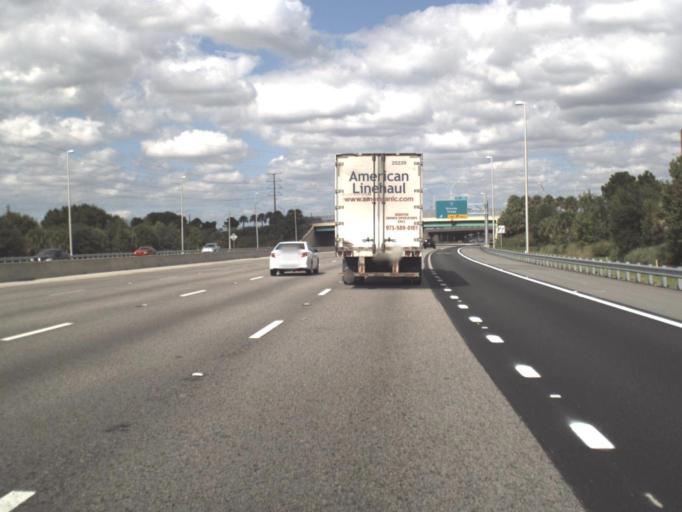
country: US
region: Florida
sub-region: Orange County
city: Tangelo Park
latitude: 28.4700
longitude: -81.4422
